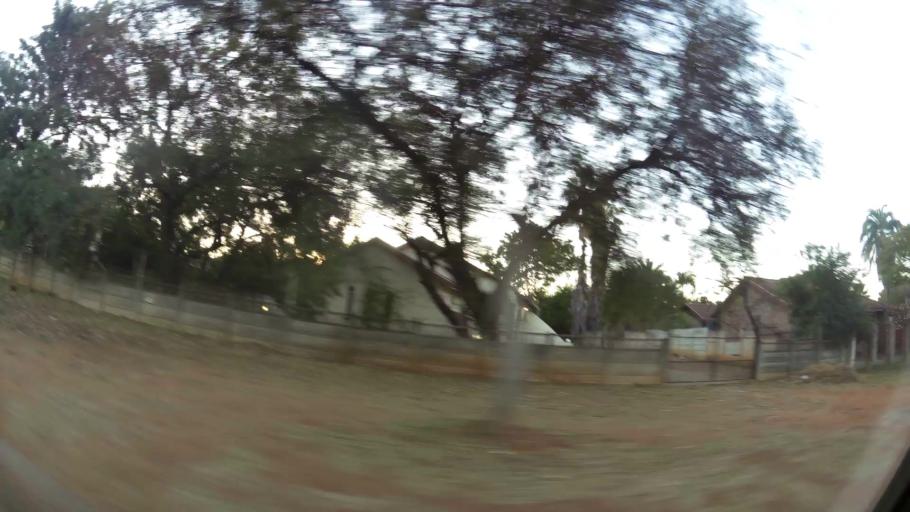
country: ZA
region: North-West
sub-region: Bojanala Platinum District Municipality
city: Rustenburg
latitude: -25.6652
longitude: 27.2154
